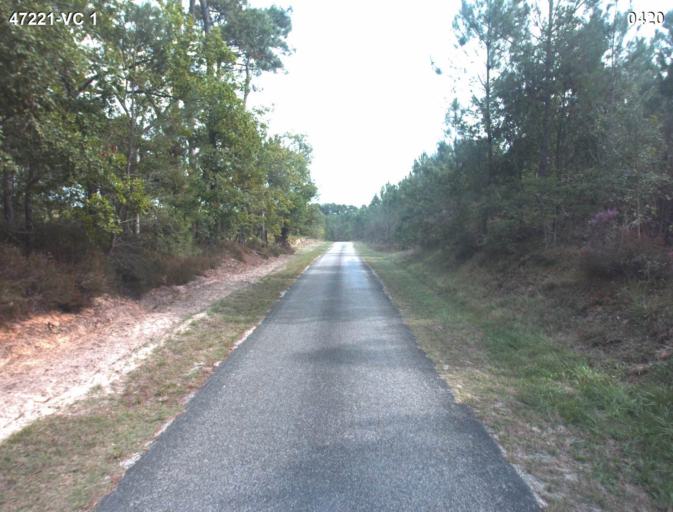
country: FR
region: Aquitaine
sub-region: Departement du Lot-et-Garonne
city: Mezin
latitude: 44.1139
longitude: 0.2230
